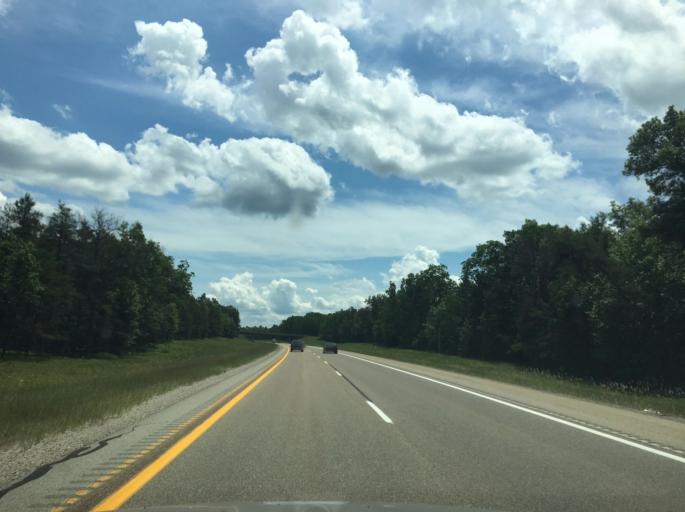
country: US
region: Michigan
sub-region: Crawford County
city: Grayling
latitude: 44.5589
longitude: -84.7075
